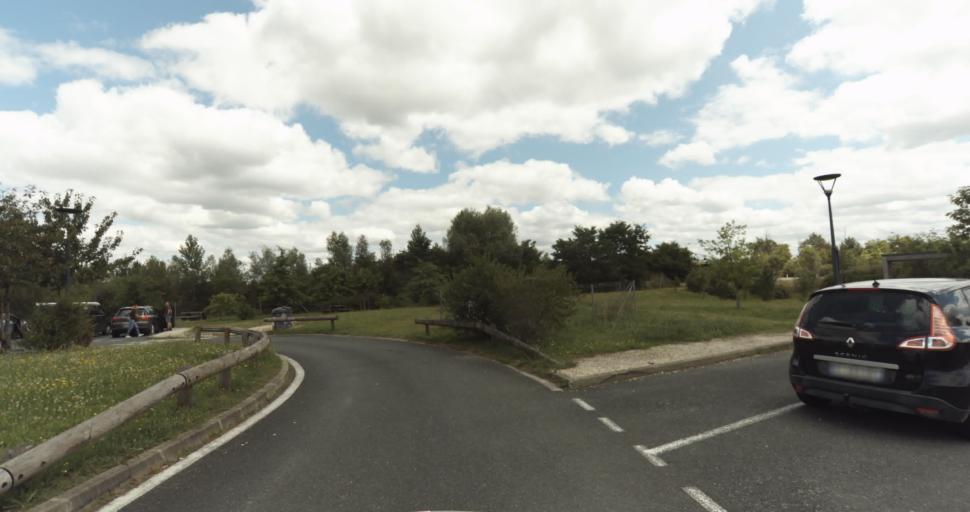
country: FR
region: Aquitaine
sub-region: Departement de la Gironde
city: Bazas
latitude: 44.4453
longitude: -0.2440
